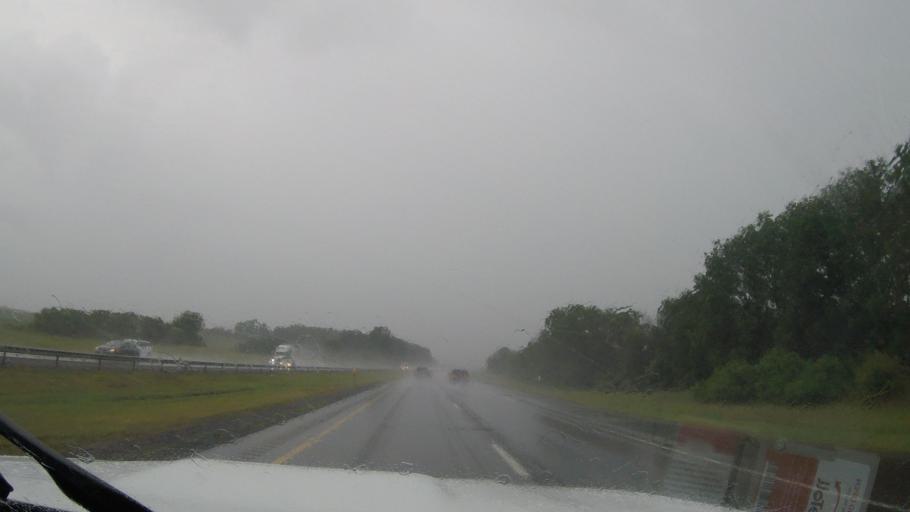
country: US
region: New York
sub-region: Ontario County
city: Phelps
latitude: 42.9670
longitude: -77.0540
